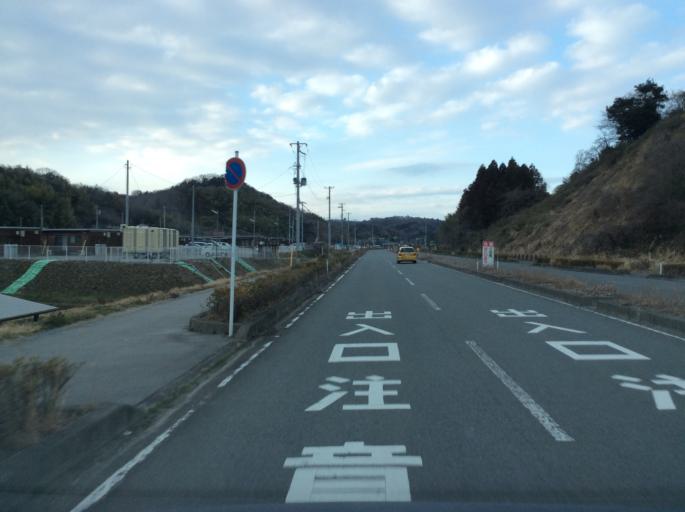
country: JP
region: Fukushima
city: Iwaki
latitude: 36.9641
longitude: 140.9193
